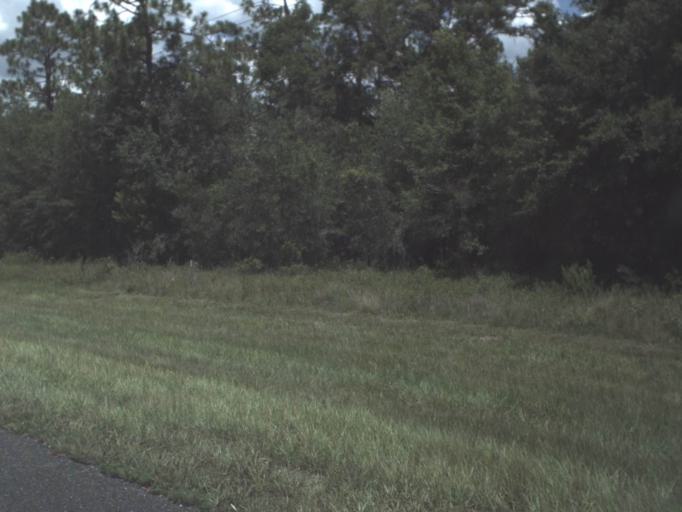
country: US
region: Florida
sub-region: Taylor County
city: Perry
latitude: 30.0460
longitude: -83.5500
